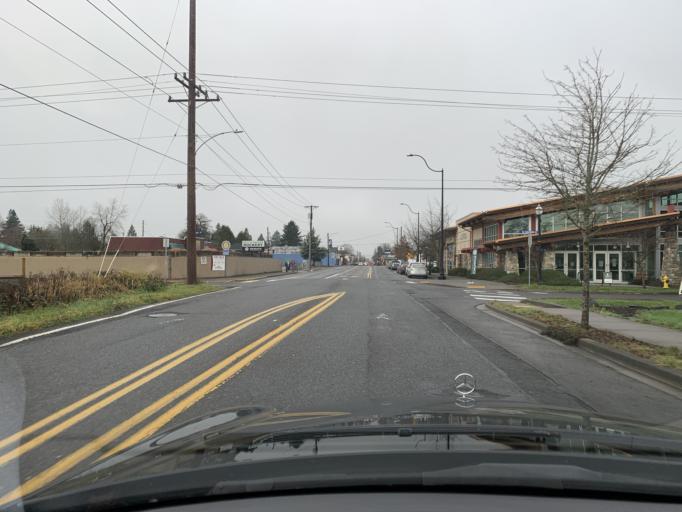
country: US
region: Washington
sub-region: Clark County
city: Battle Ground
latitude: 45.7810
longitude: -122.5265
